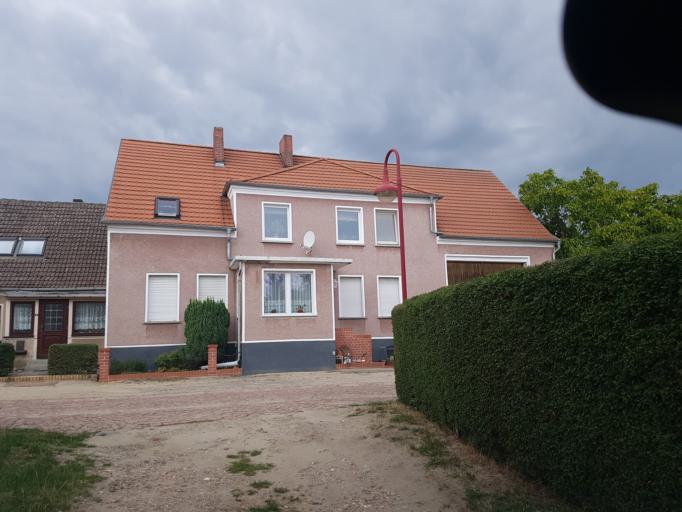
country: DE
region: Brandenburg
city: Gorzke
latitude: 52.1127
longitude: 12.3688
